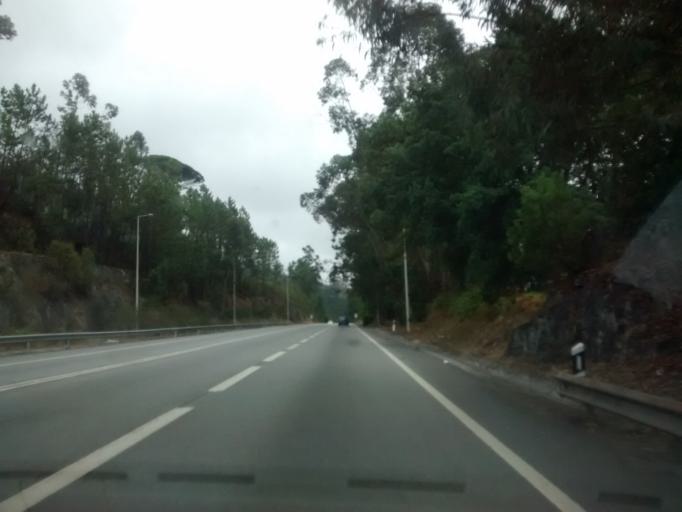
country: PT
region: Braga
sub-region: Braga
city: Oliveira
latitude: 41.5044
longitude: -8.4551
